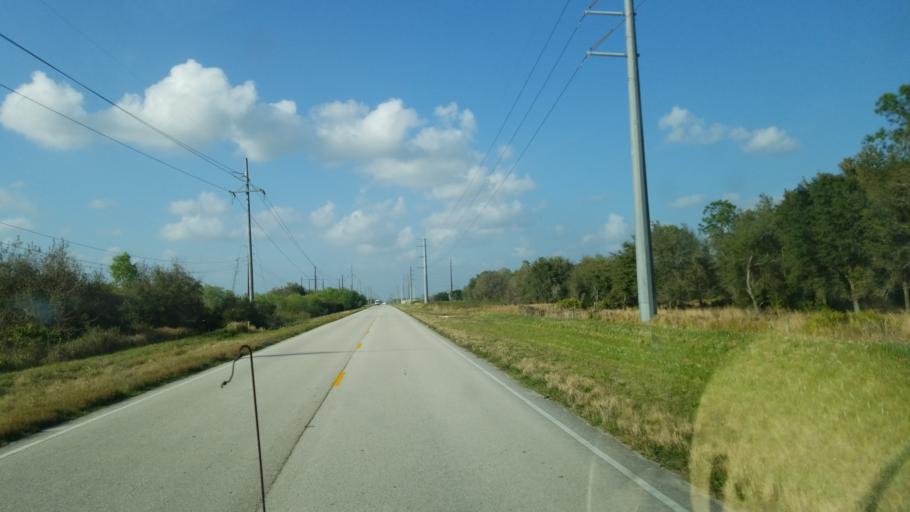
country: US
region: Florida
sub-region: Hardee County
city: Wauchula
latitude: 27.5169
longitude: -81.9256
